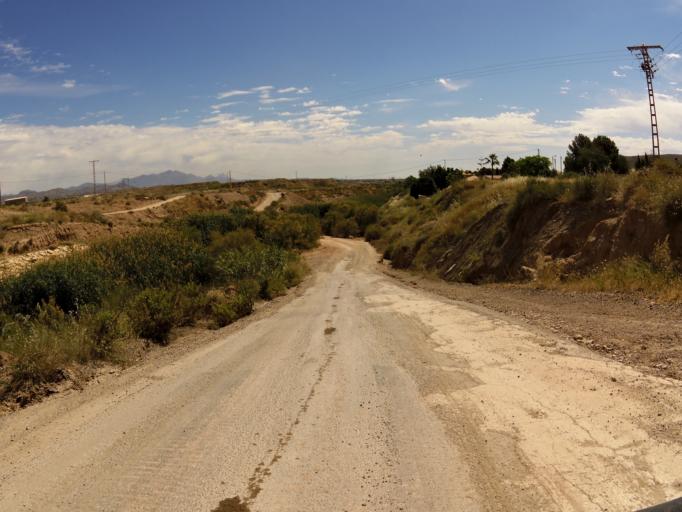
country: ES
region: Valencia
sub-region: Provincia de Alicante
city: Agost
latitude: 38.3966
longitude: -0.6098
